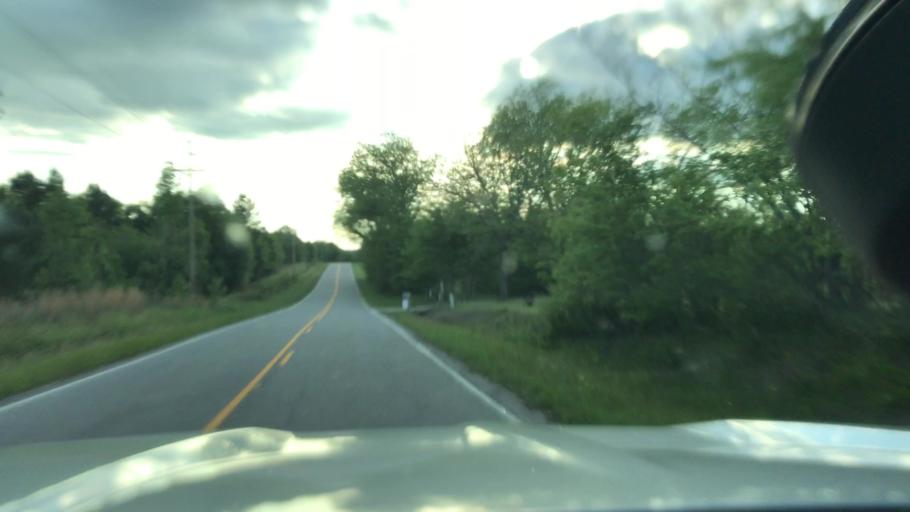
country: US
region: South Carolina
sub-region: Barnwell County
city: Blackville
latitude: 33.4737
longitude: -81.1936
